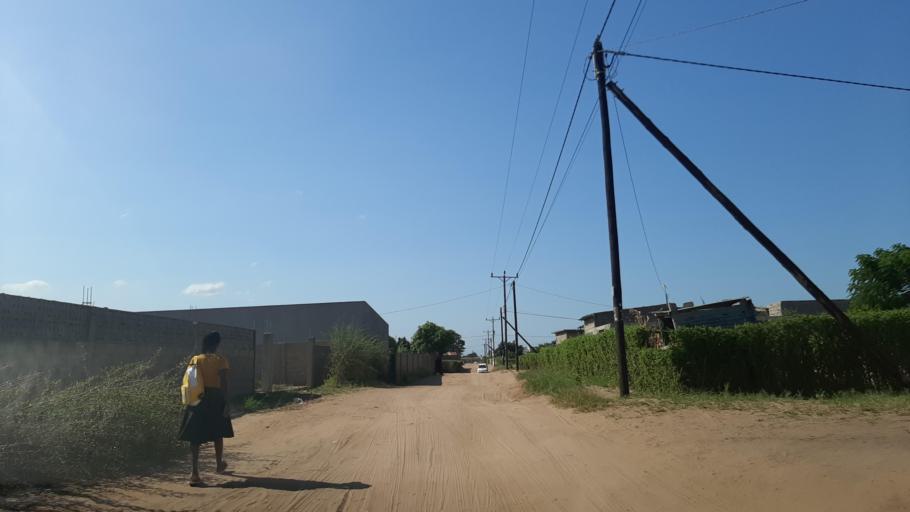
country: MZ
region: Maputo
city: Matola
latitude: -25.8027
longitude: 32.4911
